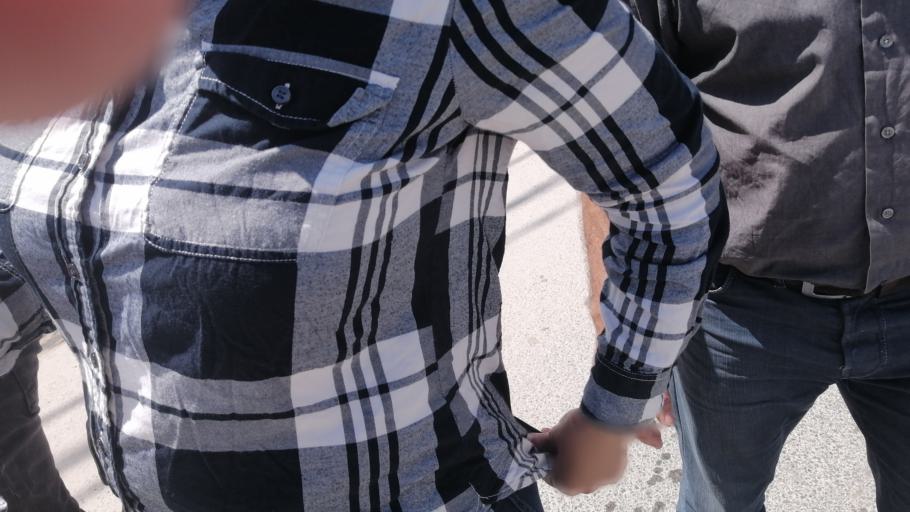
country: TN
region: Silyanah
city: Siliana
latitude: 36.0848
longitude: 9.3655
